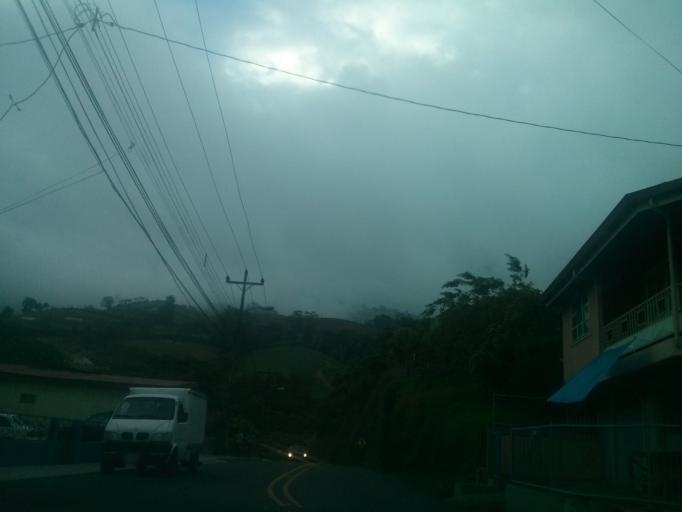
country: CR
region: Cartago
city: Cot
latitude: 9.9156
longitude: -83.8108
